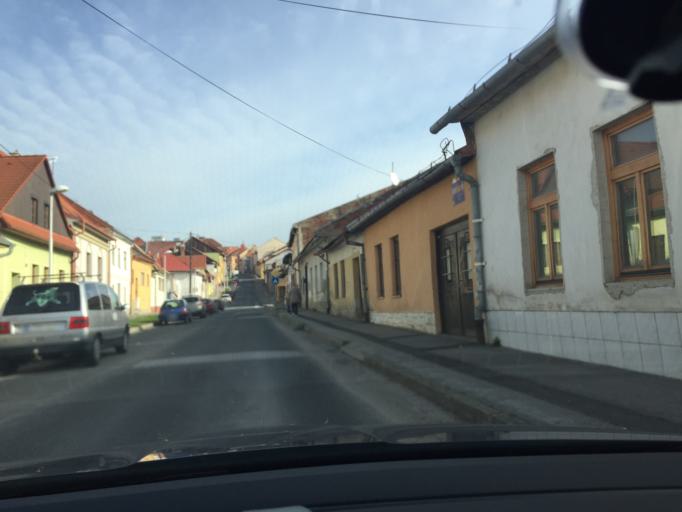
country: SK
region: Presovsky
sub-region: Okres Presov
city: Levoca
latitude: 49.0225
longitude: 20.5851
